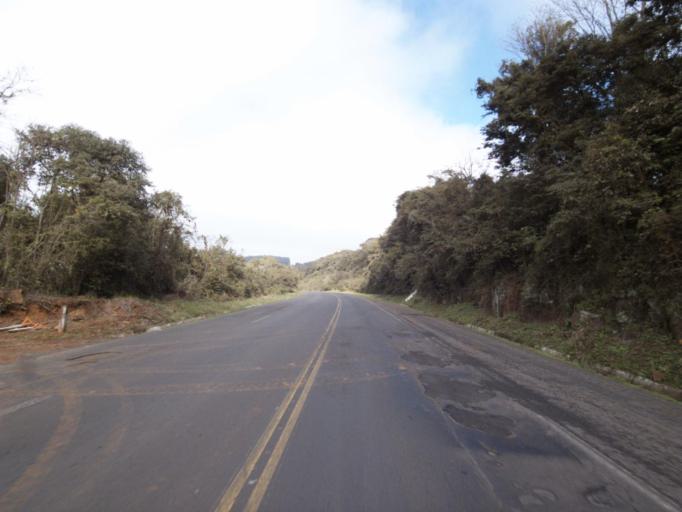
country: BR
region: Rio Grande do Sul
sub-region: Frederico Westphalen
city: Frederico Westphalen
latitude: -27.1066
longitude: -53.2150
